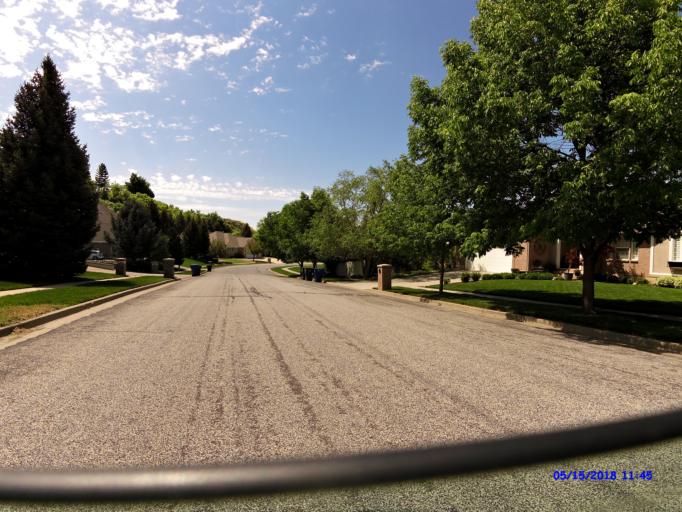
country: US
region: Utah
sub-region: Weber County
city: South Ogden
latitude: 41.1783
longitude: -111.9390
